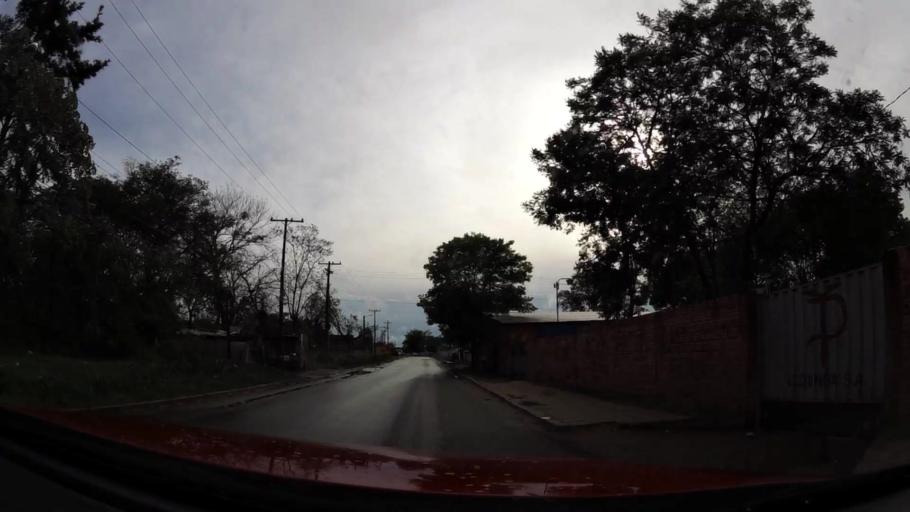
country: PY
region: Central
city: Limpio
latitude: -25.2089
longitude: -57.5086
